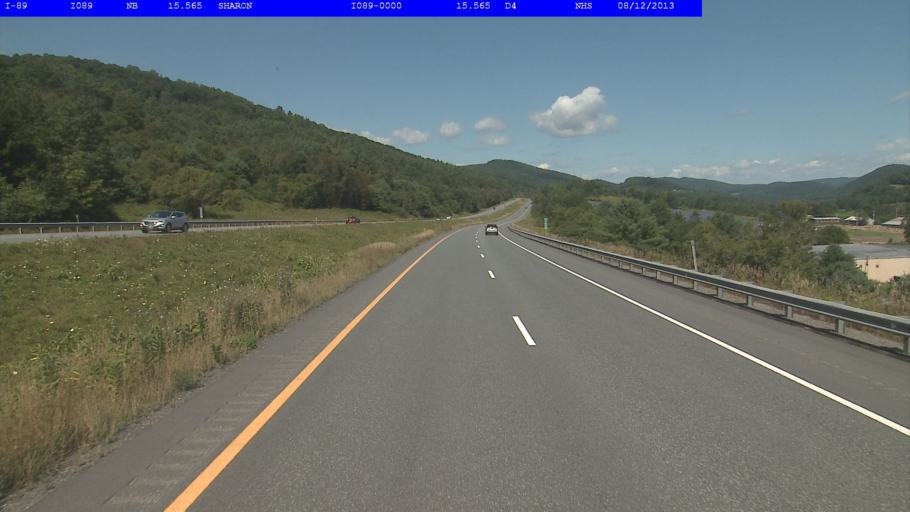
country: US
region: Vermont
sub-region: Windsor County
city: Woodstock
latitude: 43.7862
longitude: -72.4929
